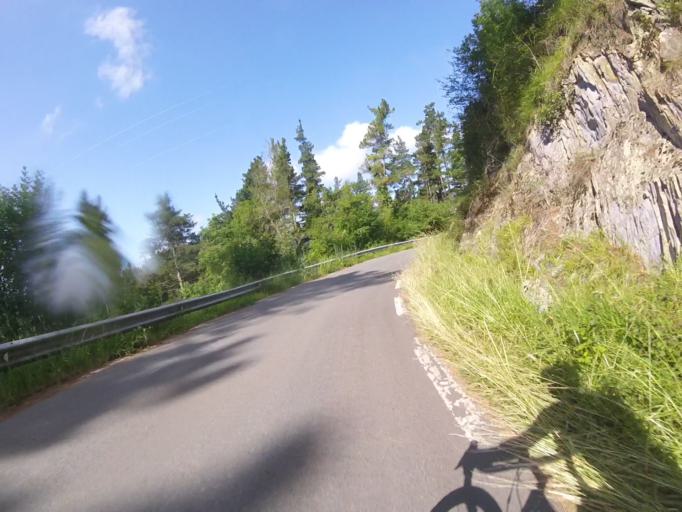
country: ES
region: Basque Country
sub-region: Provincia de Guipuzcoa
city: Beasain
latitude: 43.0811
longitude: -2.2270
